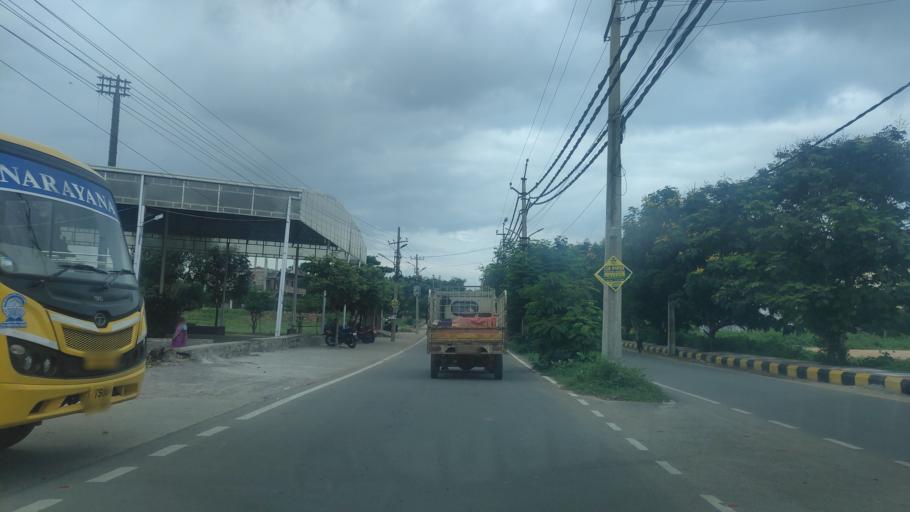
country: IN
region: Telangana
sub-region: Medak
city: Serilingampalle
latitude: 17.5052
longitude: 78.3528
